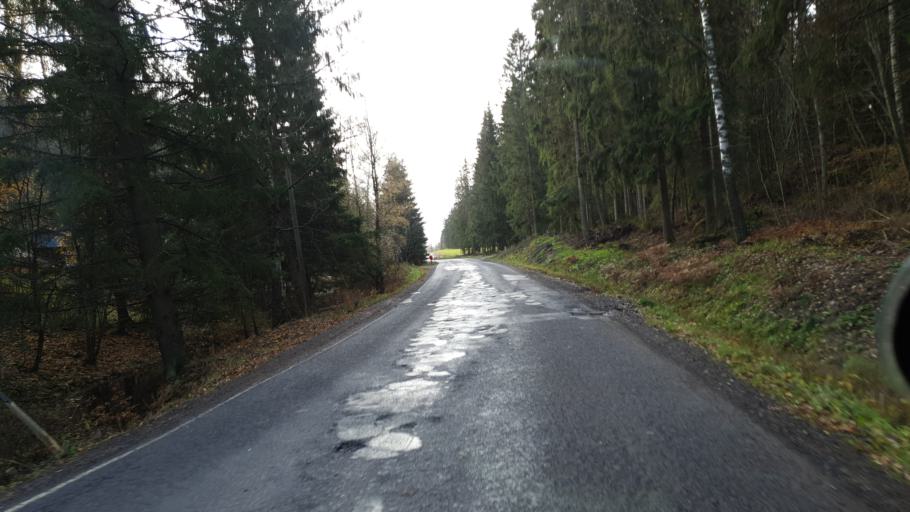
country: FI
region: Uusimaa
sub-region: Helsinki
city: Siuntio
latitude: 60.2647
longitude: 24.3036
